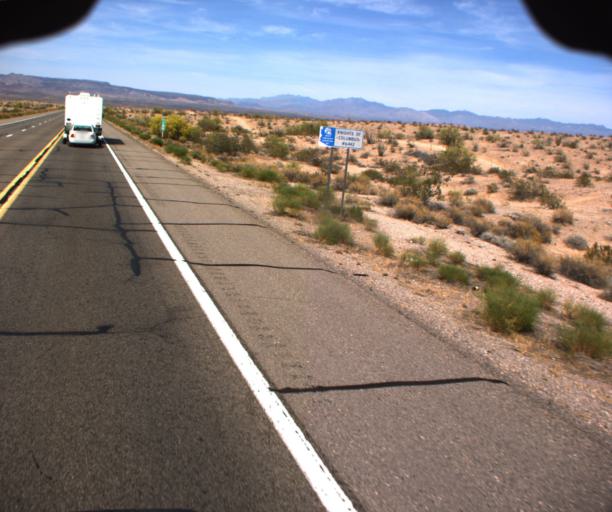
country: US
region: Arizona
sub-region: Mohave County
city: Desert Hills
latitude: 34.6744
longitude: -114.3088
